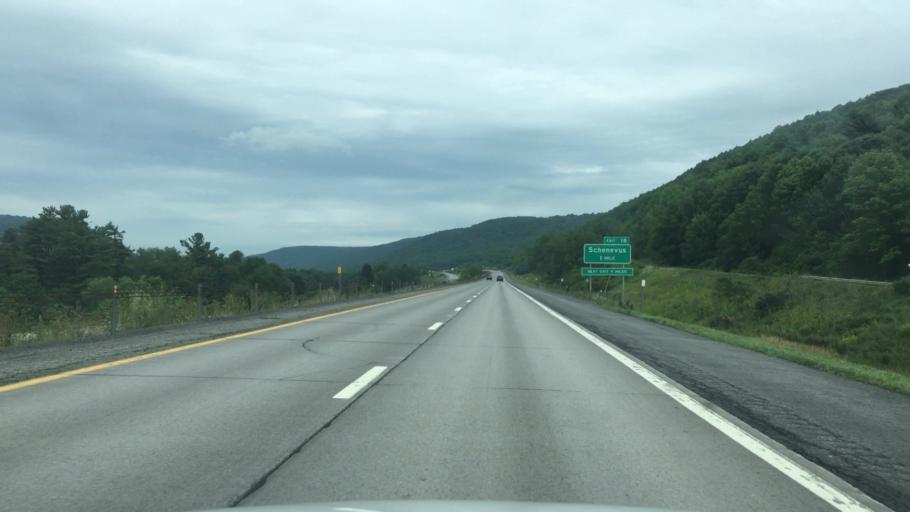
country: US
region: New York
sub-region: Otsego County
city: Worcester
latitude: 42.5373
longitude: -74.8385
